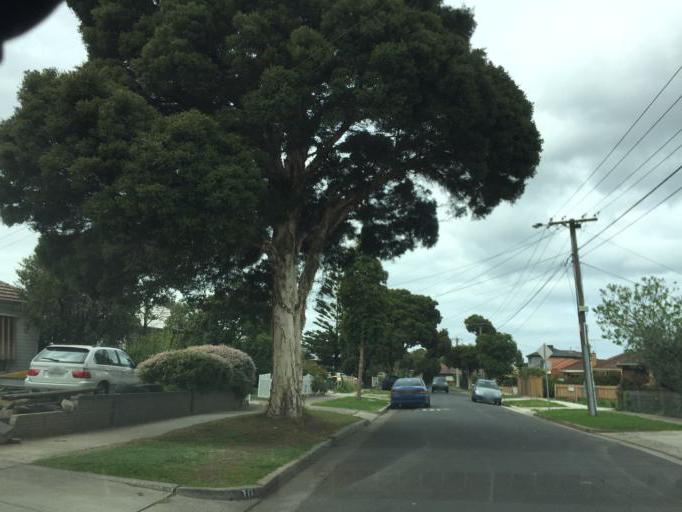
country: AU
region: Victoria
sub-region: Brimbank
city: Brooklyn
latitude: -37.8217
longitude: 144.8437
